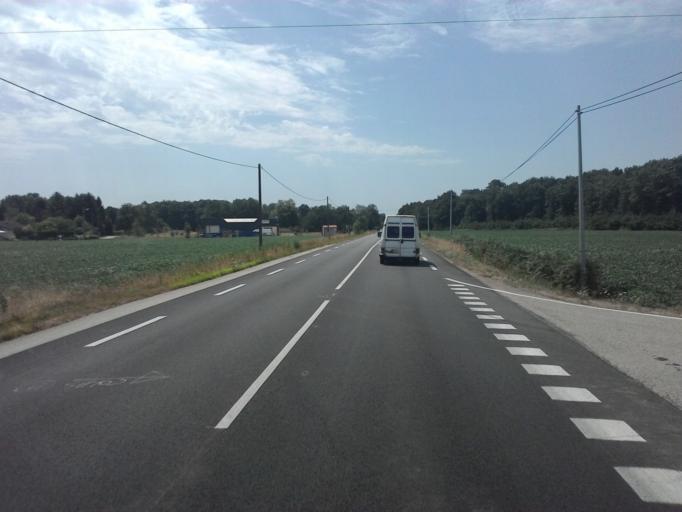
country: FR
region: Rhone-Alpes
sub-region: Departement de l'Ain
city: Saint-Etienne-du-Bois
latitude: 46.2657
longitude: 5.2811
